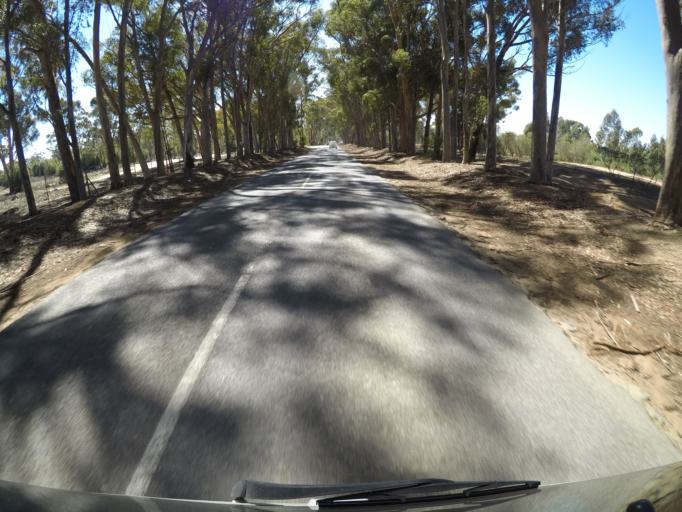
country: ZA
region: Western Cape
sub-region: City of Cape Town
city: Sunset Beach
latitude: -33.7577
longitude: 18.5541
